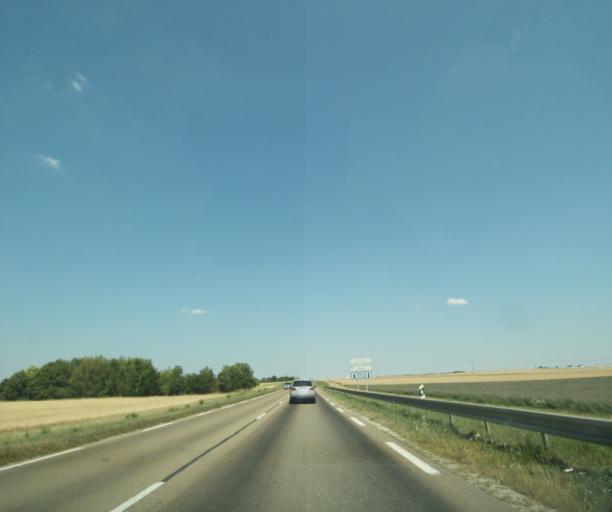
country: FR
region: Champagne-Ardenne
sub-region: Departement de la Marne
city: Sarry
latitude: 48.9178
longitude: 4.4219
